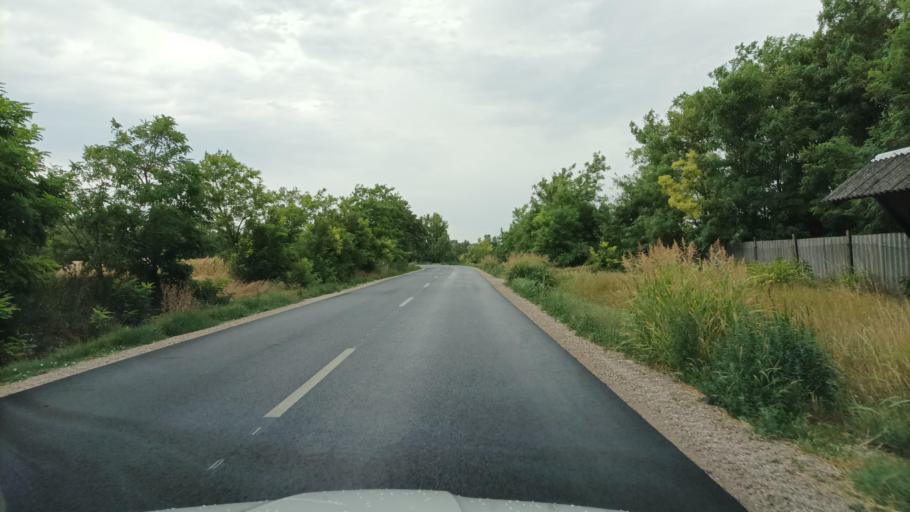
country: HU
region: Pest
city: Dabas
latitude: 47.2040
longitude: 19.2678
